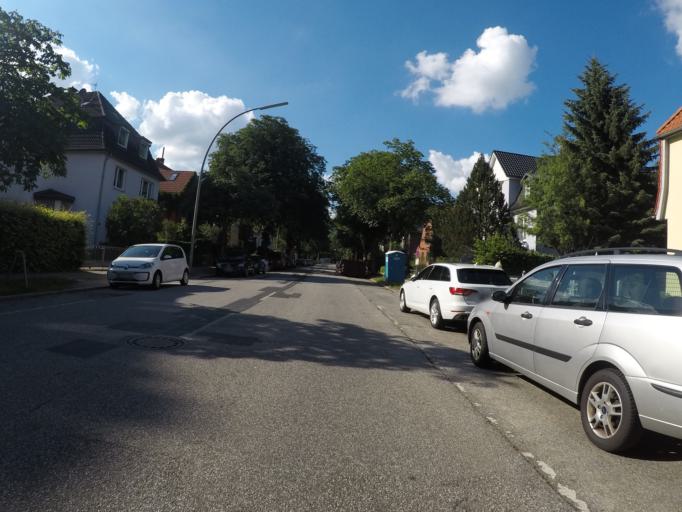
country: DE
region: Hamburg
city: Fuhlsbuettel
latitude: 53.6339
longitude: 10.0257
